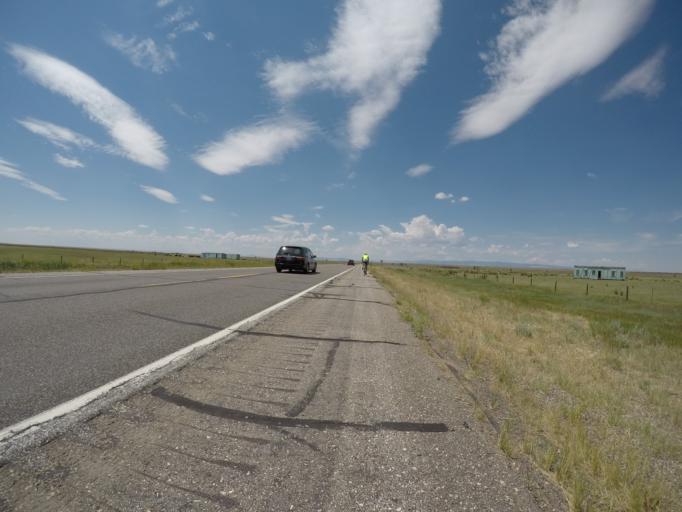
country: US
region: Wyoming
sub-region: Albany County
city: Laramie
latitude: 41.5583
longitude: -105.6727
